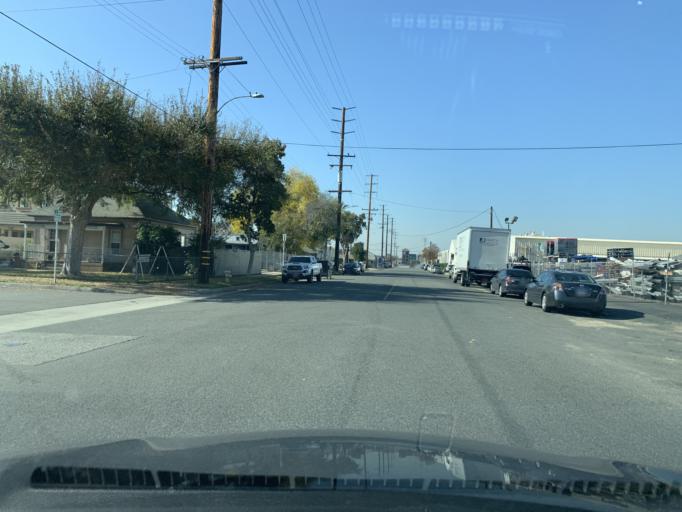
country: US
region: California
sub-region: Los Angeles County
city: Covina
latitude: 34.0916
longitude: -117.8854
